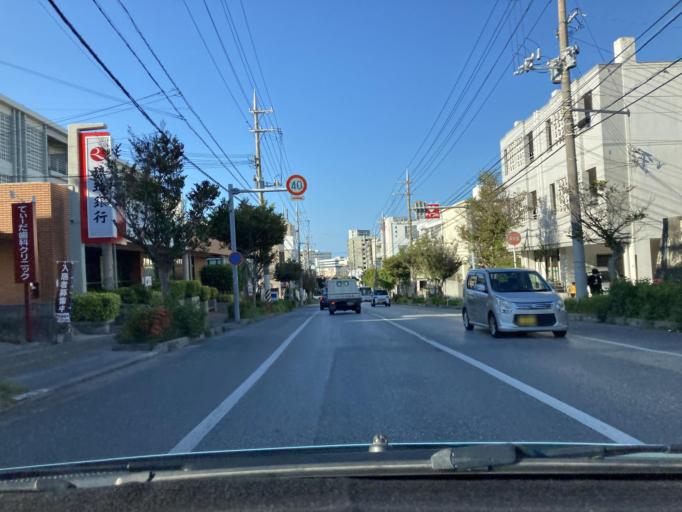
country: JP
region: Okinawa
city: Ginowan
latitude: 26.2544
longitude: 127.7138
